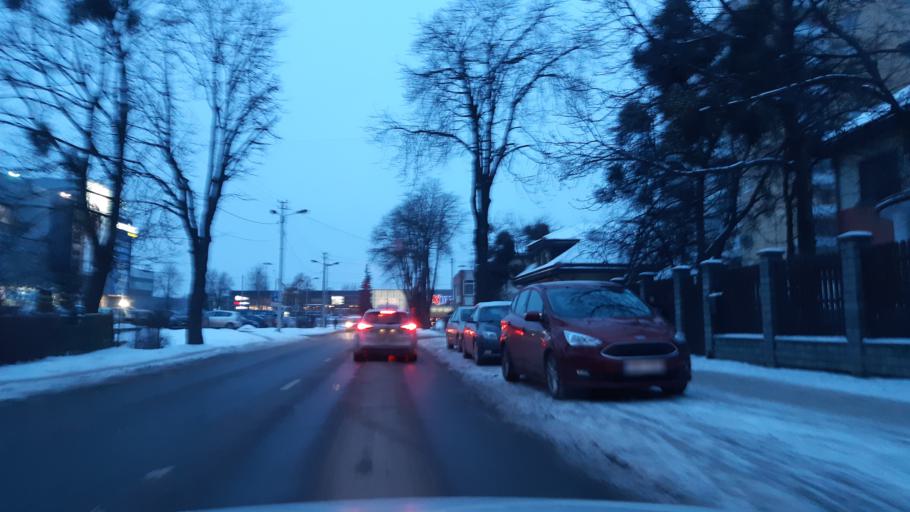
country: LT
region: Kauno apskritis
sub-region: Kaunas
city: Eiguliai
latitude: 54.9127
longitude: 23.9412
